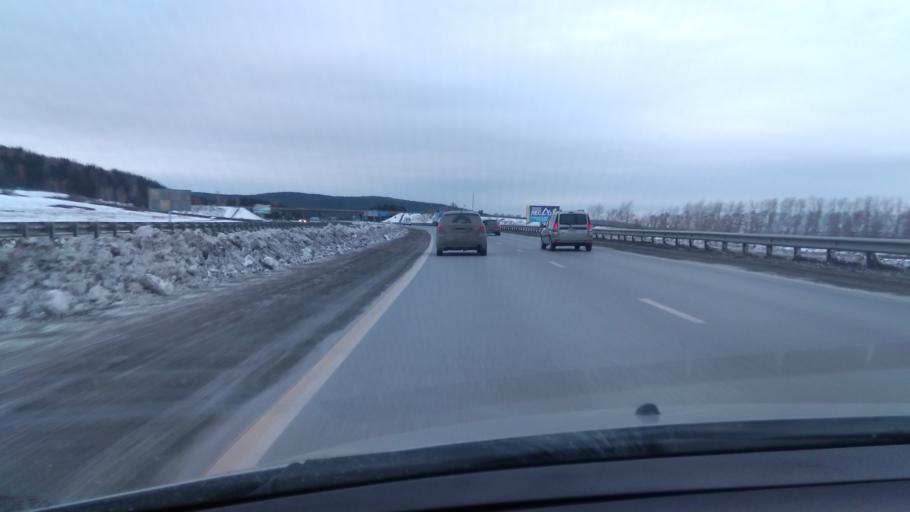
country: RU
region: Sverdlovsk
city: Aramil
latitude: 56.6915
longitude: 60.7624
